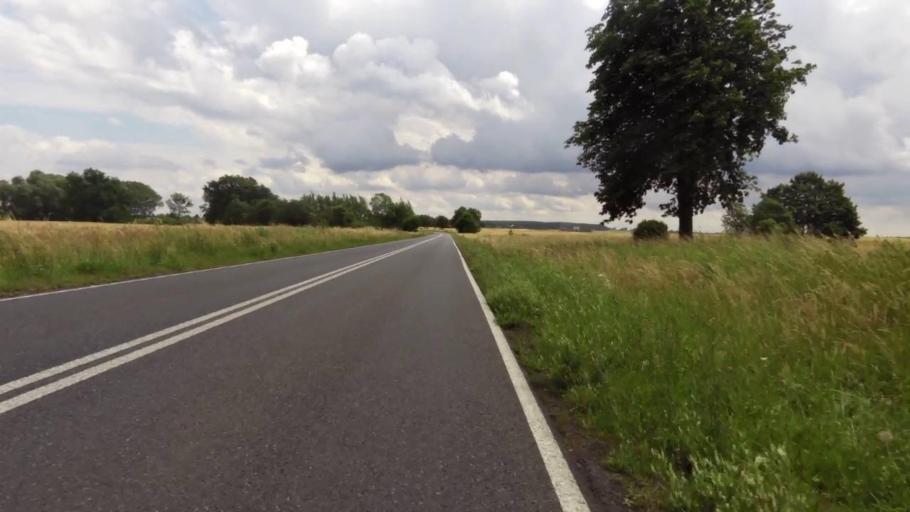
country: PL
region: West Pomeranian Voivodeship
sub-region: Powiat pyrzycki
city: Lipiany
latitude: 52.9979
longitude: 15.0414
